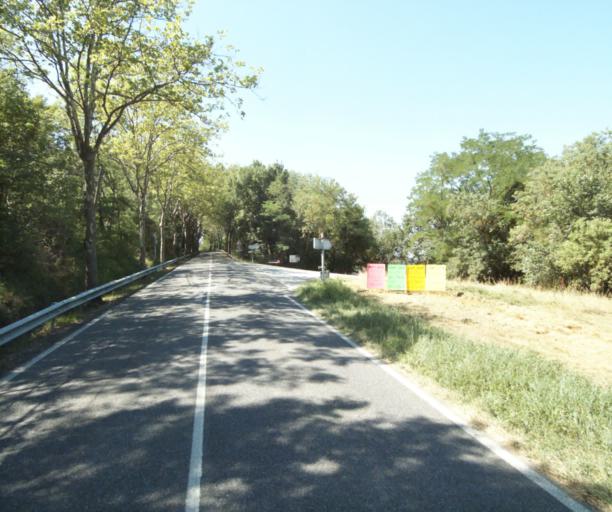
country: FR
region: Midi-Pyrenees
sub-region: Departement de la Haute-Garonne
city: Saint-Felix-Lauragais
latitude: 43.4927
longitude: 1.9009
